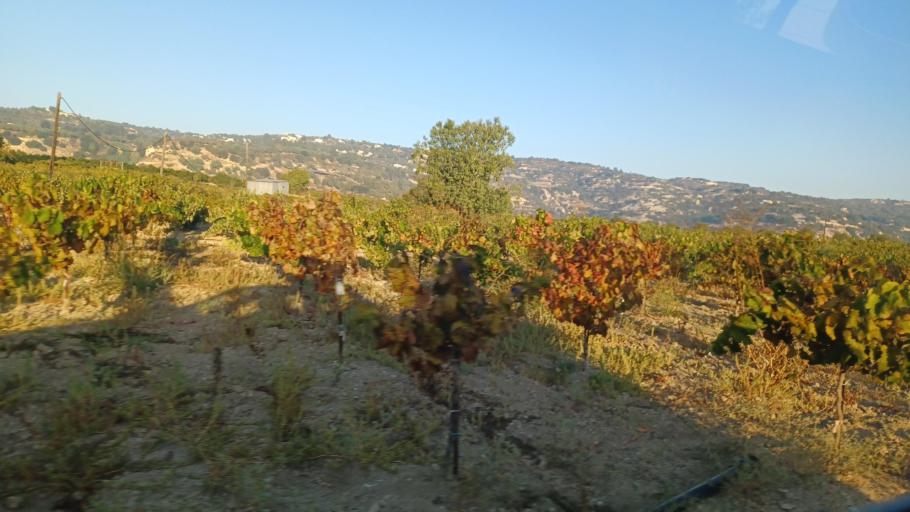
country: CY
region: Pafos
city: Mesogi
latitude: 34.8468
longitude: 32.5168
